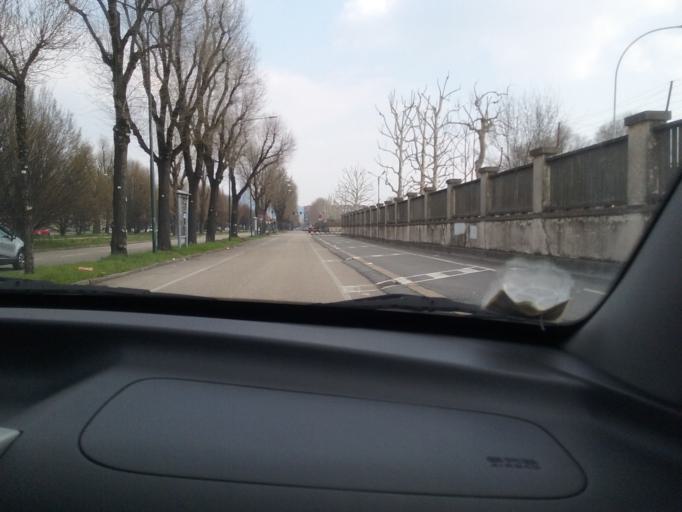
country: IT
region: Piedmont
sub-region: Provincia di Torino
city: Gerbido
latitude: 45.0333
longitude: 7.6311
